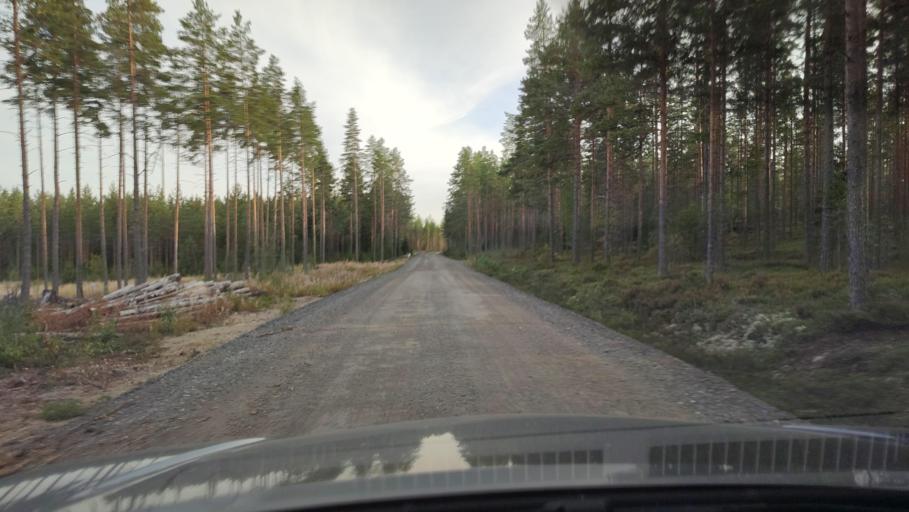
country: FI
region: Southern Ostrobothnia
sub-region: Suupohja
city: Karijoki
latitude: 62.1523
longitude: 21.6179
